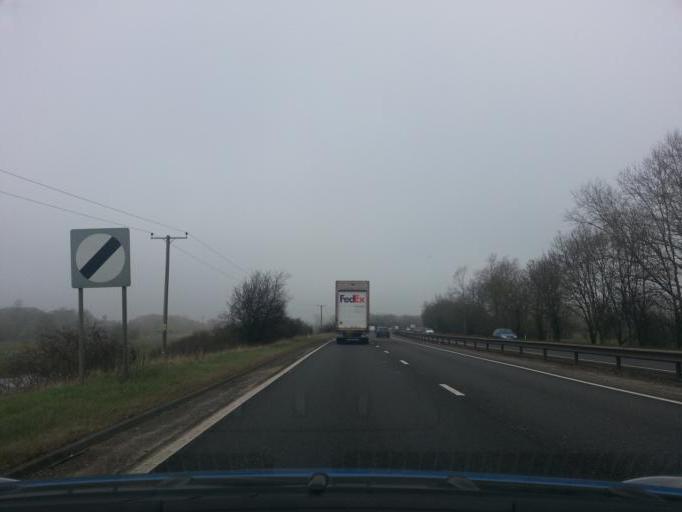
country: GB
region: England
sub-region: Oxfordshire
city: Yarnton
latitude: 51.7695
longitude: -1.3024
